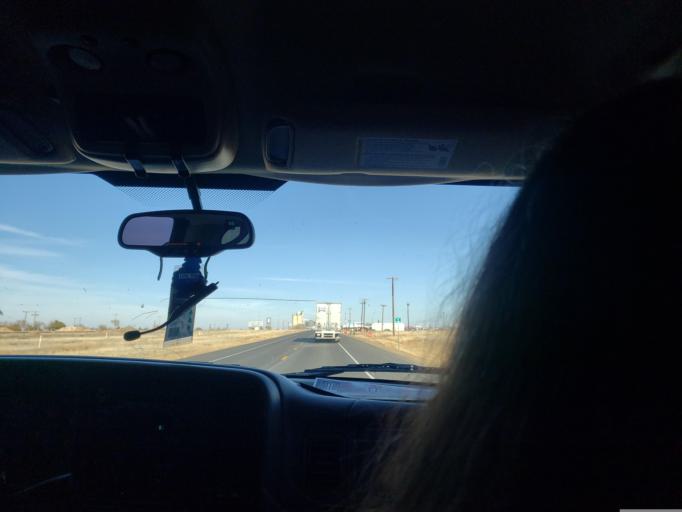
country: US
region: Texas
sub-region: Sherman County
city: Stratford
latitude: 36.3272
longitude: -102.0810
